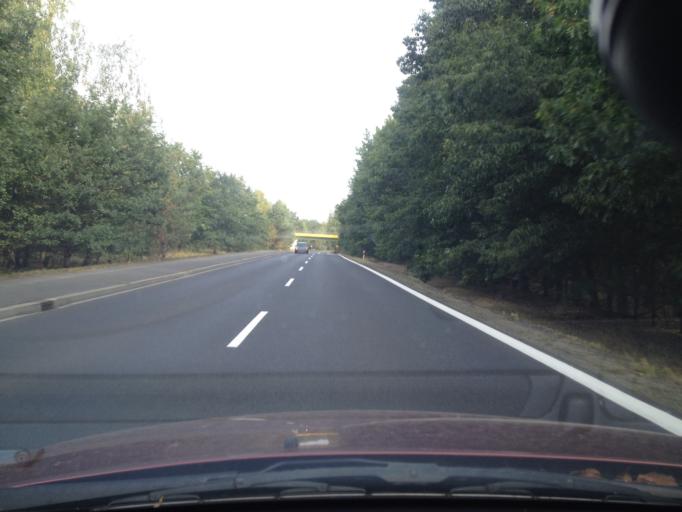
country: PL
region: Lubusz
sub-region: Powiat zaganski
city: Szprotawa
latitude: 51.4409
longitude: 15.6008
